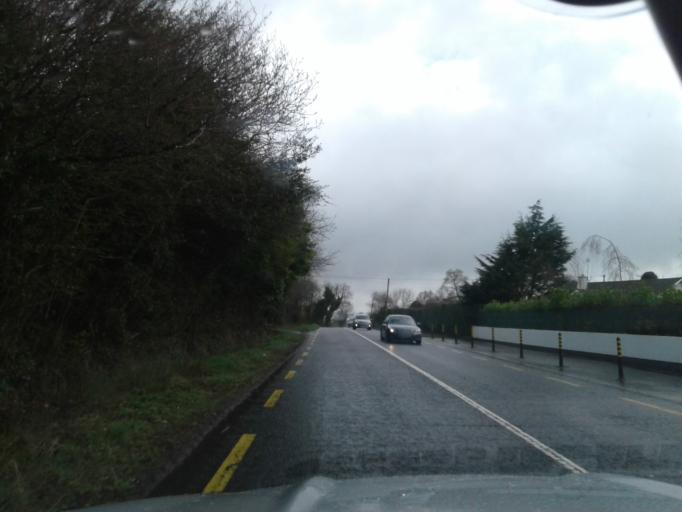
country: IE
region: Ulster
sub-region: County Donegal
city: Letterkenny
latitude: 54.9732
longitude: -7.6873
